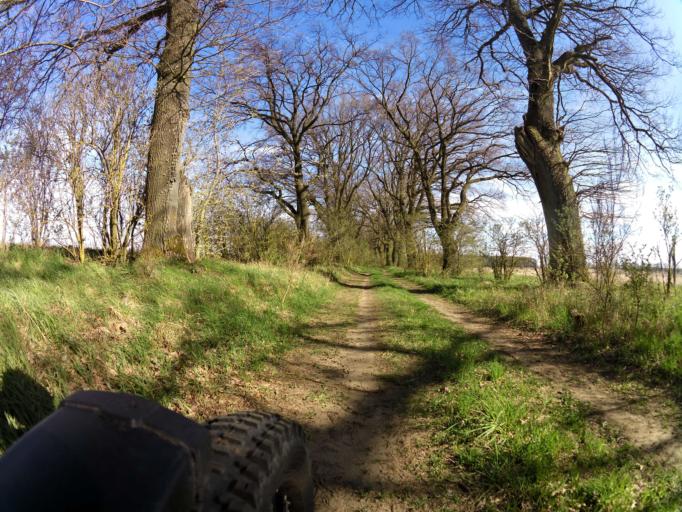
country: PL
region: West Pomeranian Voivodeship
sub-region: Powiat lobeski
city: Resko
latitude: 53.7821
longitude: 15.5505
